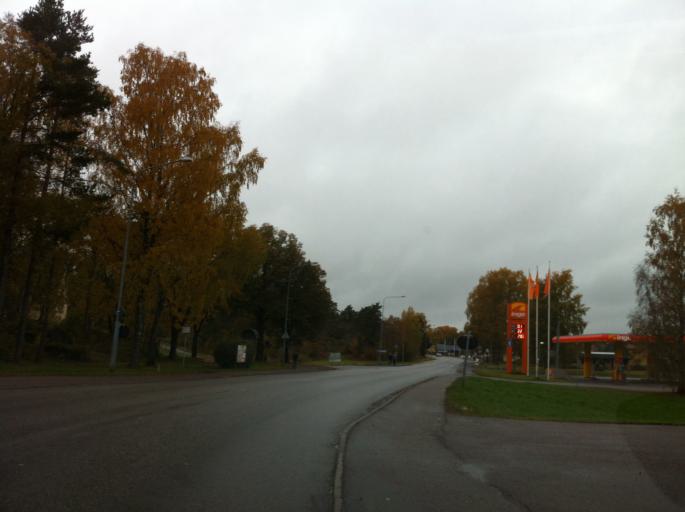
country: SE
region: Uppsala
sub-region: Osthammars Kommun
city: OEsthammar
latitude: 60.2590
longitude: 18.3667
